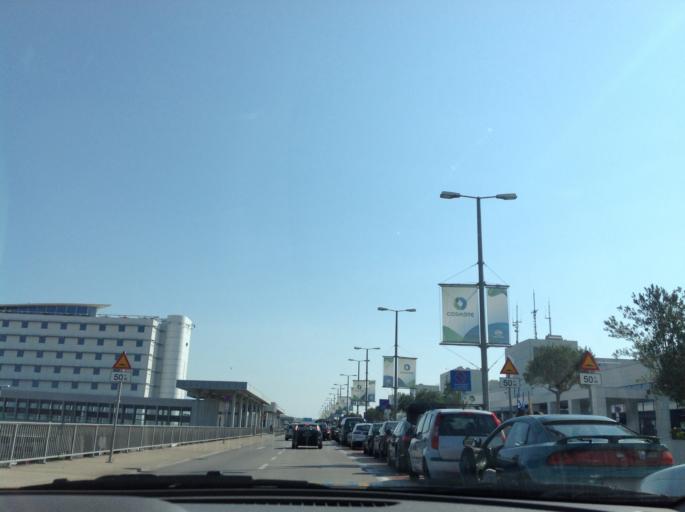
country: GR
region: Attica
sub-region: Nomarchia Anatolikis Attikis
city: Spata
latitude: 37.9353
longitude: 23.9452
